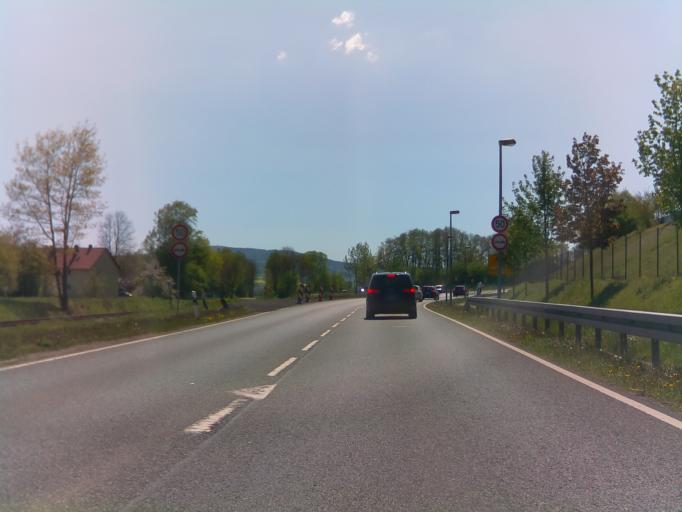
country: DE
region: Hesse
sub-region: Regierungsbezirk Kassel
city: Bad Hersfeld
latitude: 50.8473
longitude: 9.6828
